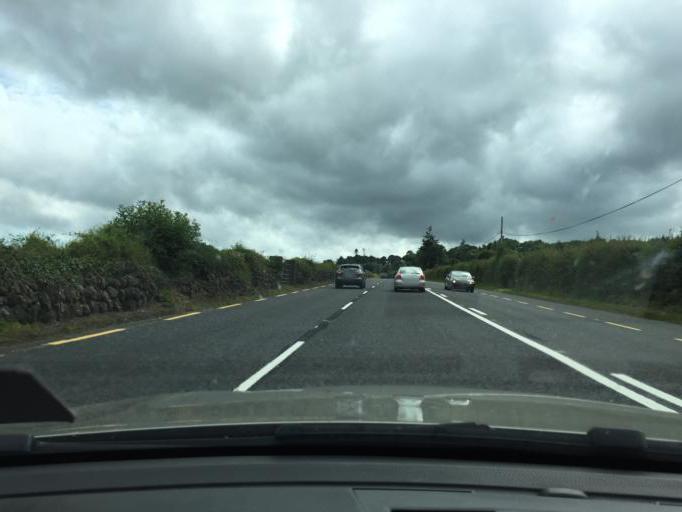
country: IE
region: Munster
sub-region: Waterford
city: Dungarvan
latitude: 52.1522
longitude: -7.5365
